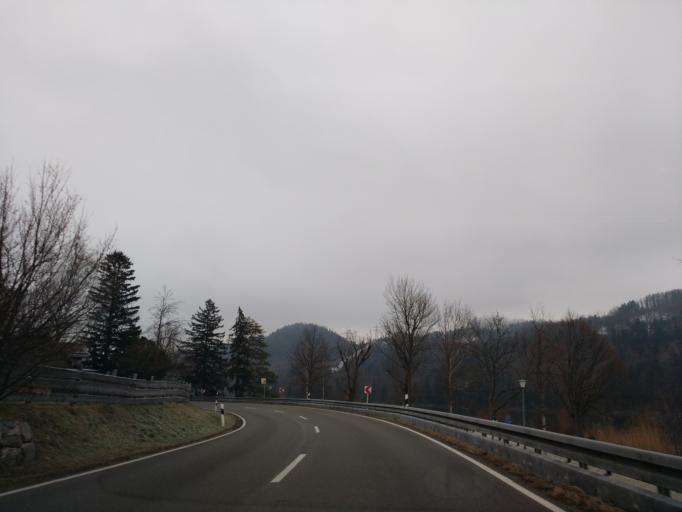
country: AT
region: Tyrol
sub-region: Politischer Bezirk Reutte
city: Vils
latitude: 47.5731
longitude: 10.6463
